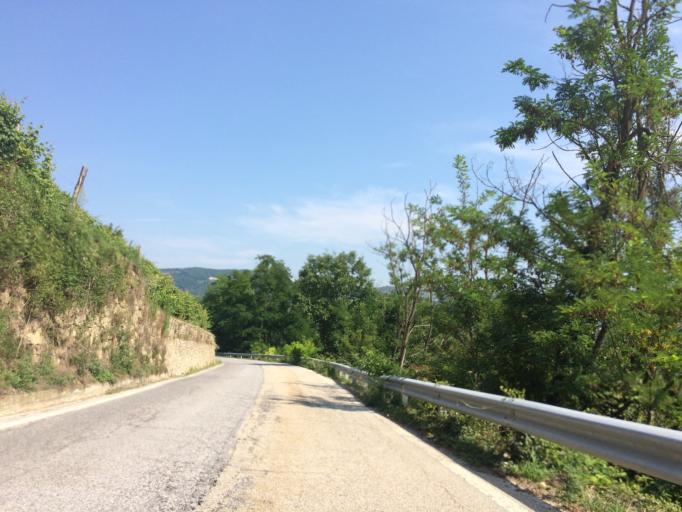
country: IT
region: Piedmont
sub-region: Provincia di Cuneo
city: Torre Bormida
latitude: 44.5705
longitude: 8.1480
